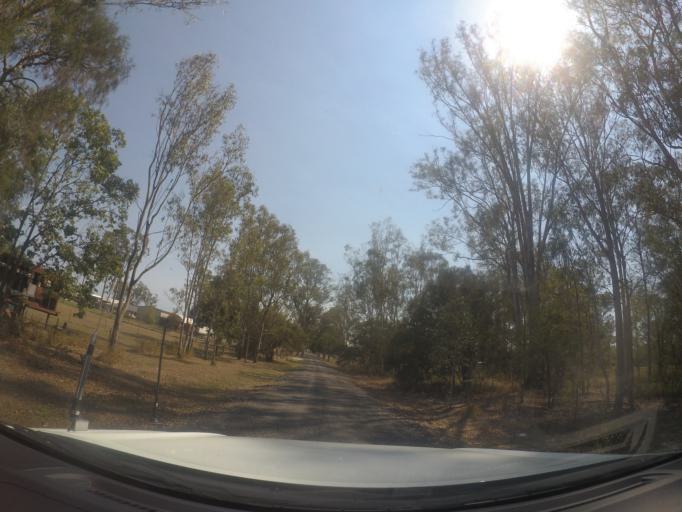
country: AU
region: Queensland
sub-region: Logan
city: North Maclean
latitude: -27.7887
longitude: 153.0275
